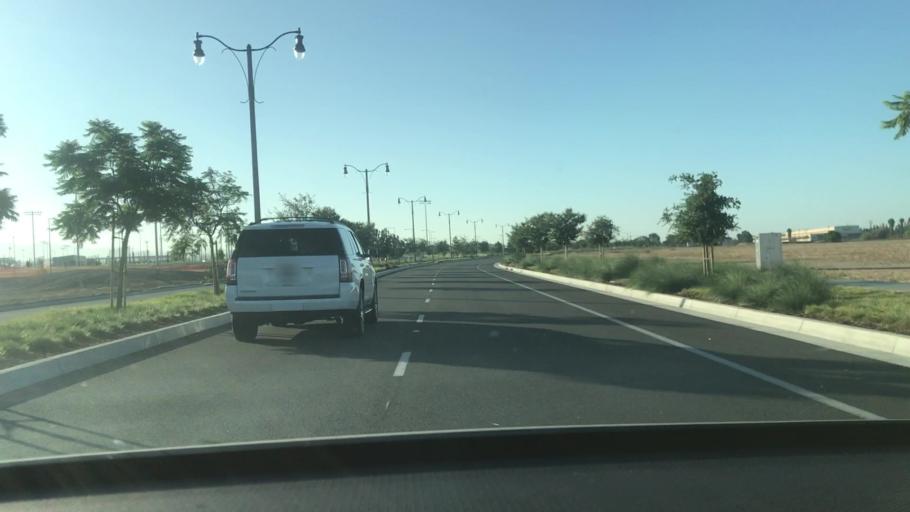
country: US
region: California
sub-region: Orange County
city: Lake Forest
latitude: 33.6713
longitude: -117.7478
